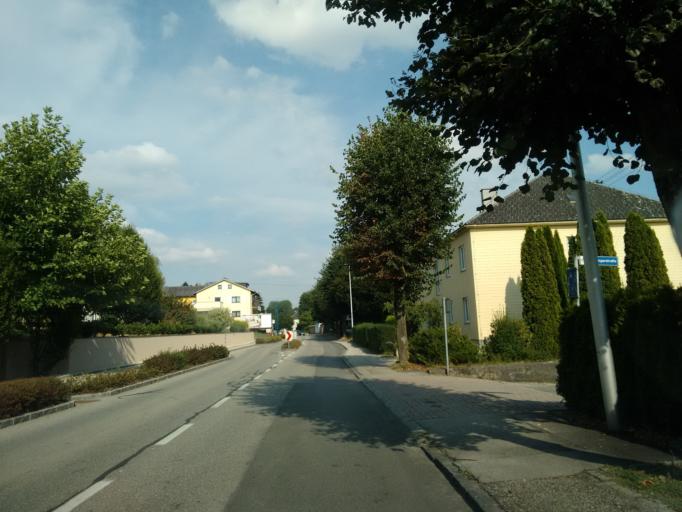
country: AT
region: Upper Austria
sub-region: Politischer Bezirk Grieskirchen
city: Bad Schallerbach
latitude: 48.2303
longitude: 13.9117
